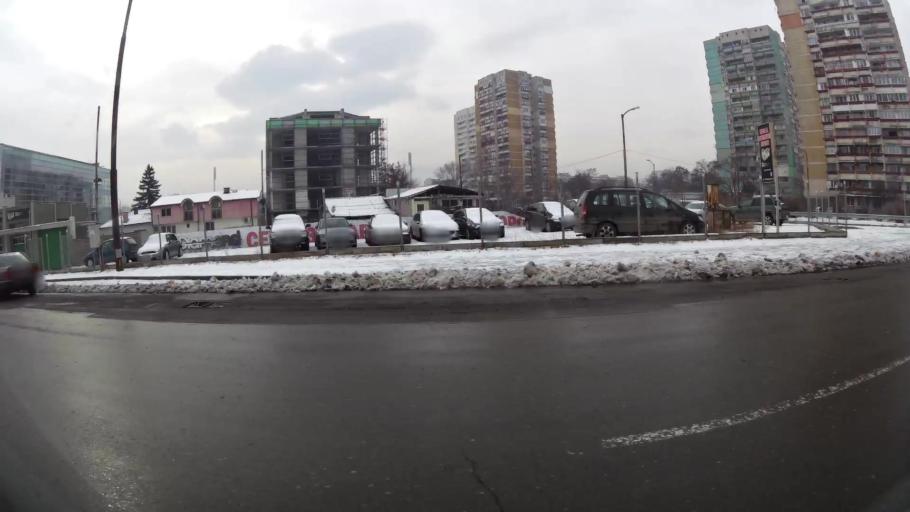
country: BG
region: Sofia-Capital
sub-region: Stolichna Obshtina
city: Sofia
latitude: 42.7101
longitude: 23.3642
